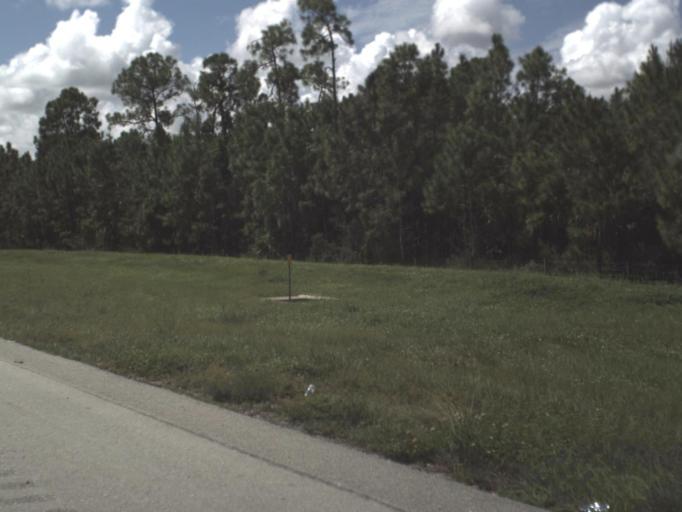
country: US
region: Florida
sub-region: Lee County
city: Estero
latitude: 26.4455
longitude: -81.7829
